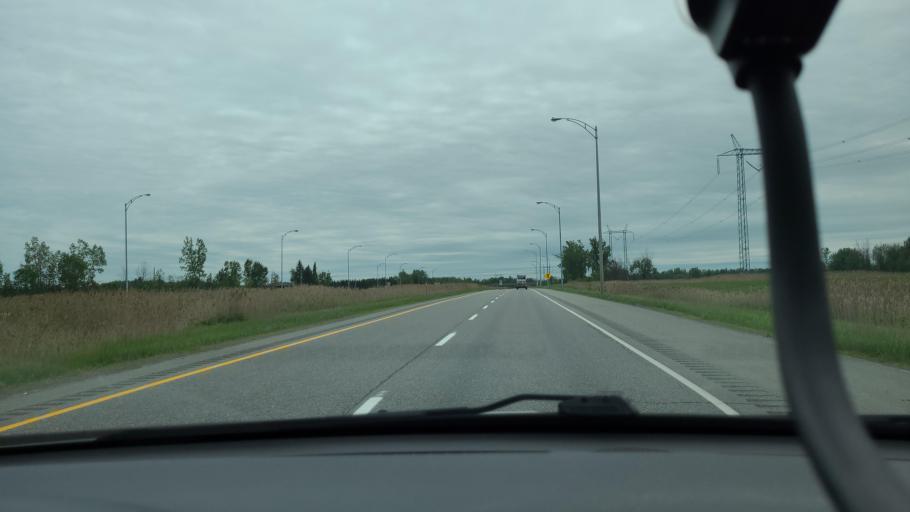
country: CA
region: Quebec
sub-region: Lanaudiere
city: Mascouche
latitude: 45.7886
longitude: -73.5793
